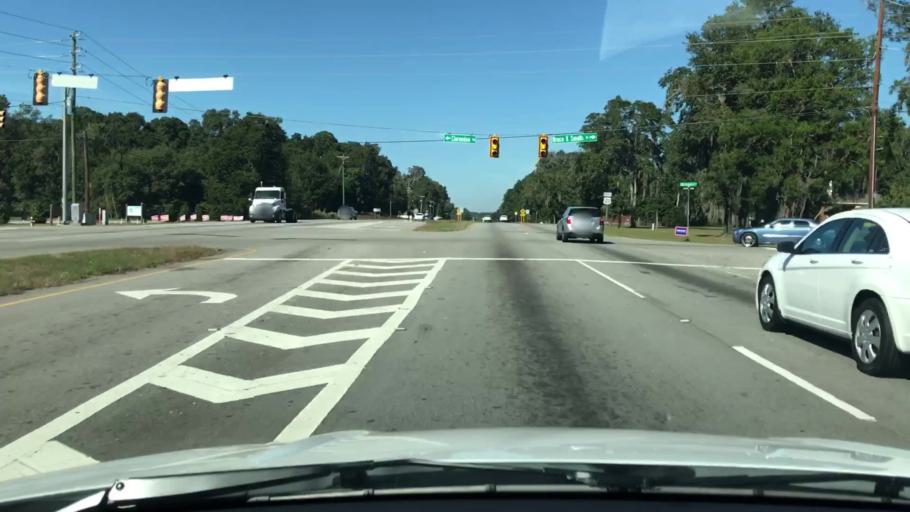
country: US
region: South Carolina
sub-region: Beaufort County
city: Burton
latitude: 32.4928
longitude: -80.7419
